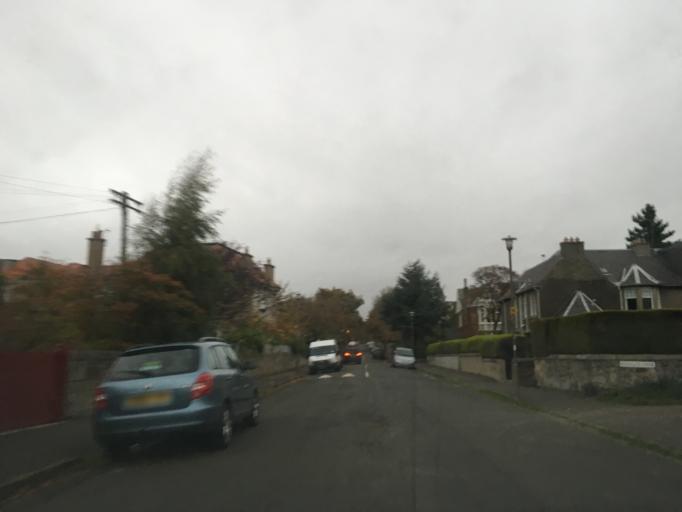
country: GB
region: Scotland
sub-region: Edinburgh
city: Edinburgh
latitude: 55.9289
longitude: -3.1845
